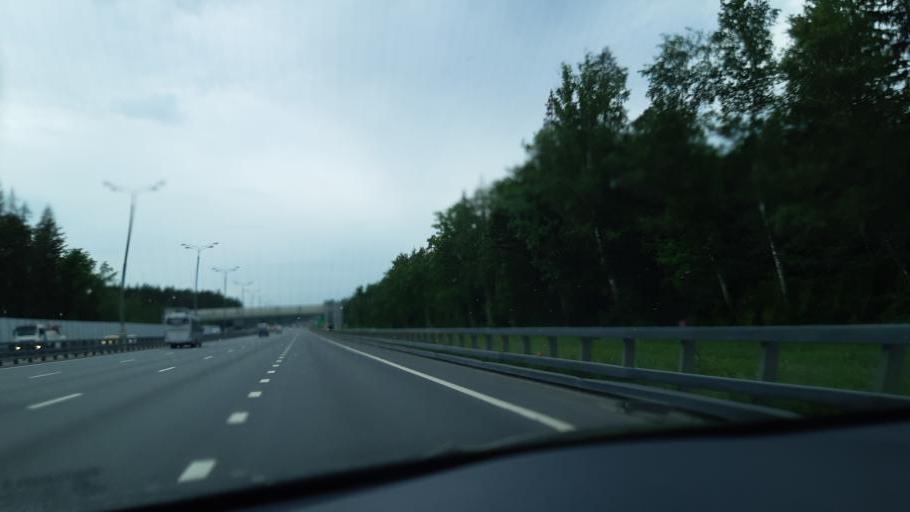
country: RU
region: Moskovskaya
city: Kokoshkino
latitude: 55.5550
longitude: 37.1417
